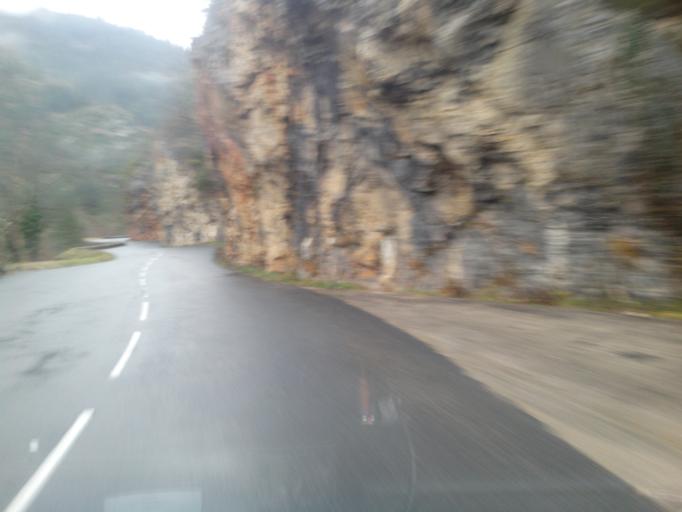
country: FR
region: Languedoc-Roussillon
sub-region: Departement de la Lozere
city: Chanac
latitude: 44.3440
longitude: 3.3887
